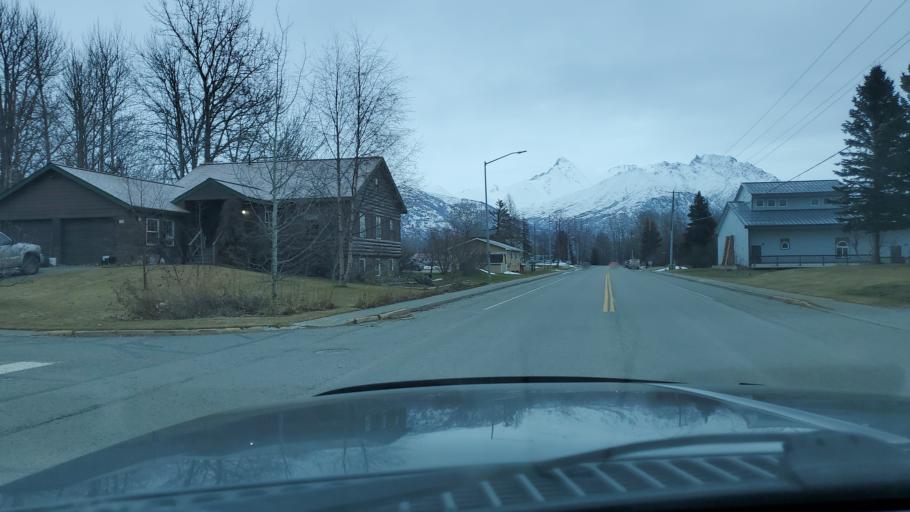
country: US
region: Alaska
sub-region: Matanuska-Susitna Borough
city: Palmer
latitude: 61.5978
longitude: -149.1085
